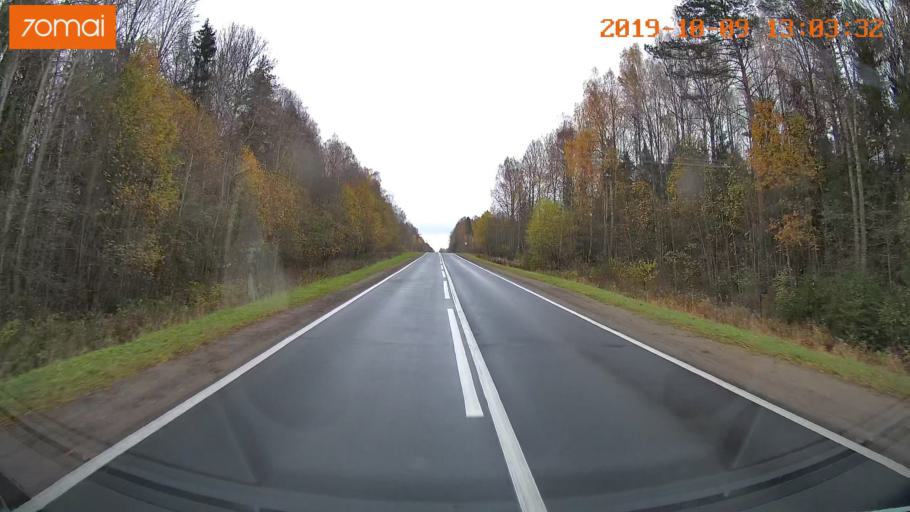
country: RU
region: Jaroslavl
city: Lyubim
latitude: 58.3594
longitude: 40.5286
